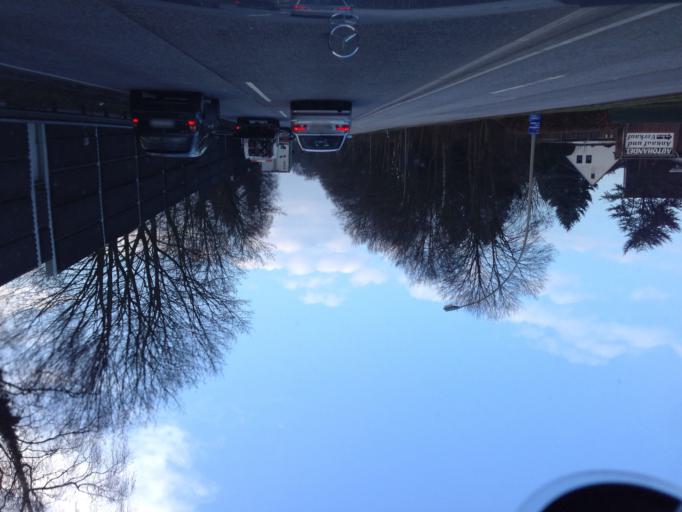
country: DE
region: Schleswig-Holstein
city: Oststeinbek
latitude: 53.5137
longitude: 10.1686
